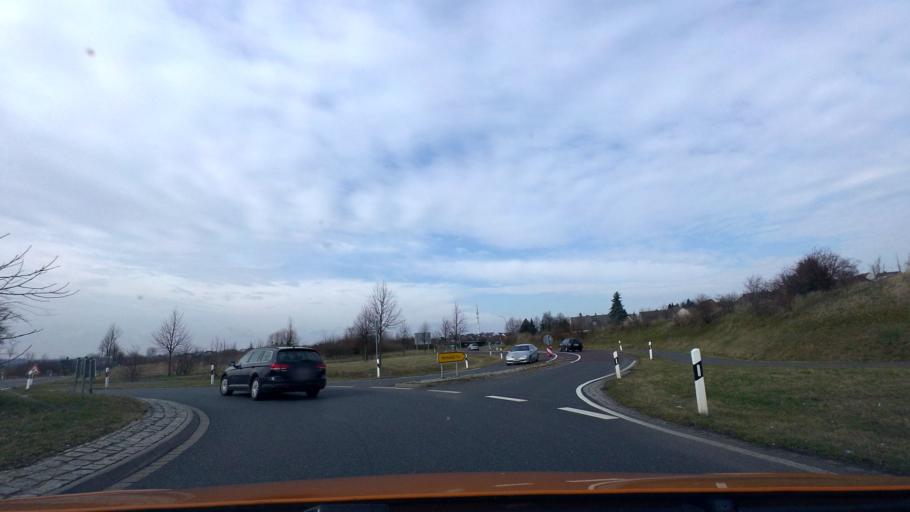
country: DE
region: Lower Saxony
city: Helmstedt
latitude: 52.2145
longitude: 11.0212
